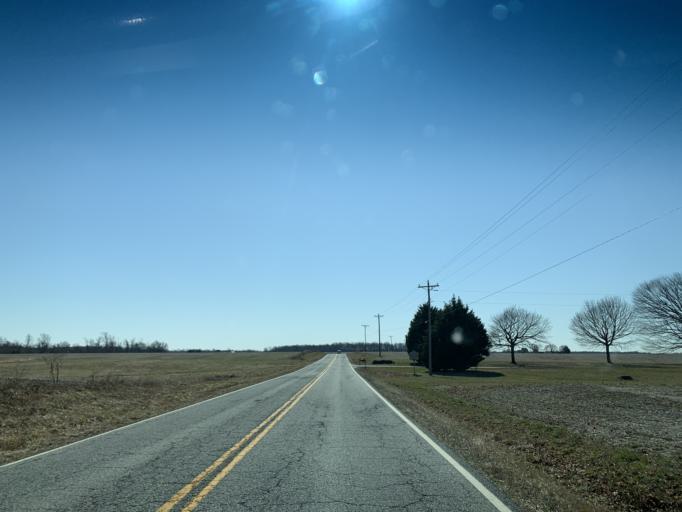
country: US
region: Maryland
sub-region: Cecil County
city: Charlestown
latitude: 39.4452
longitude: -75.9026
